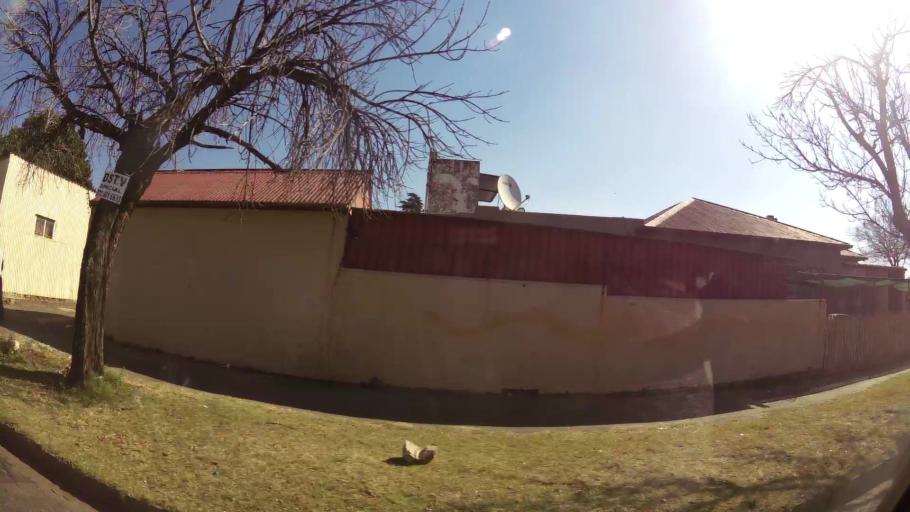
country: ZA
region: Gauteng
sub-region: City of Johannesburg Metropolitan Municipality
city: Johannesburg
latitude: -26.2489
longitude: 28.0450
